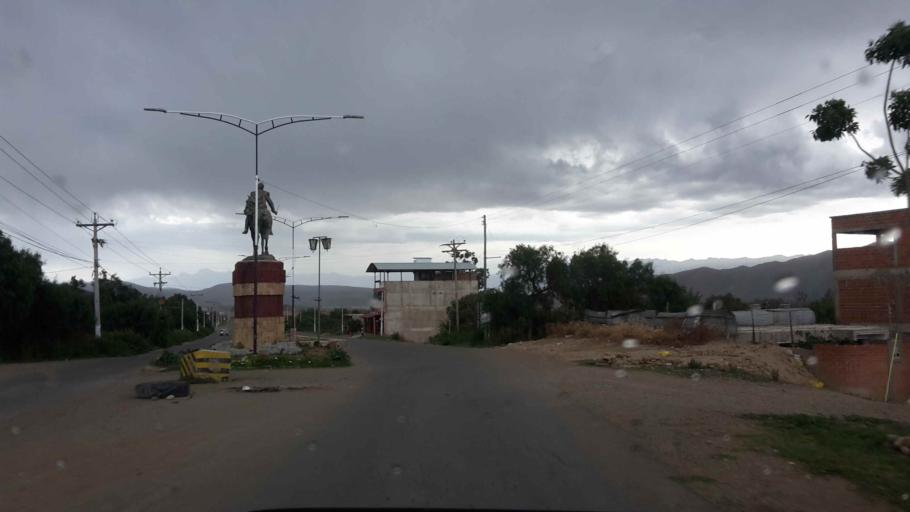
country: BO
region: Cochabamba
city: Tarata
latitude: -17.6054
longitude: -66.0305
